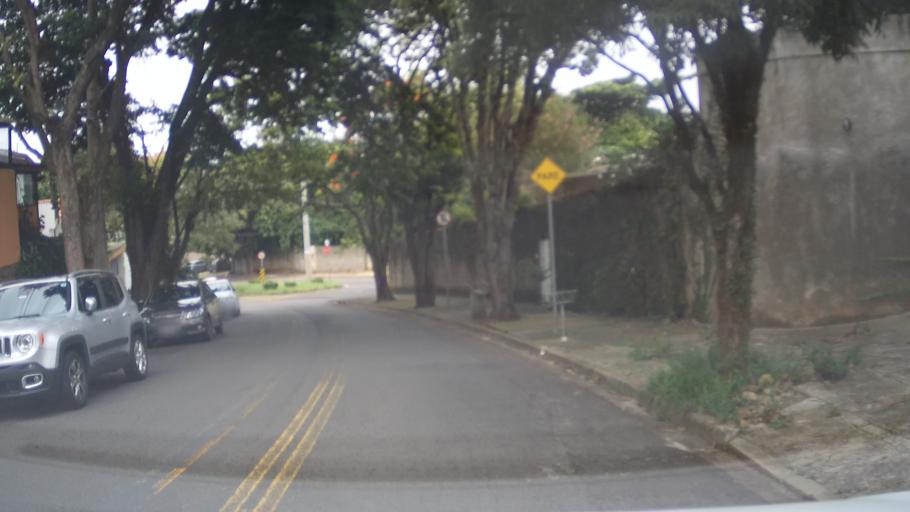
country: BR
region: Sao Paulo
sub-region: Campinas
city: Campinas
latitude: -22.8986
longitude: -47.0383
